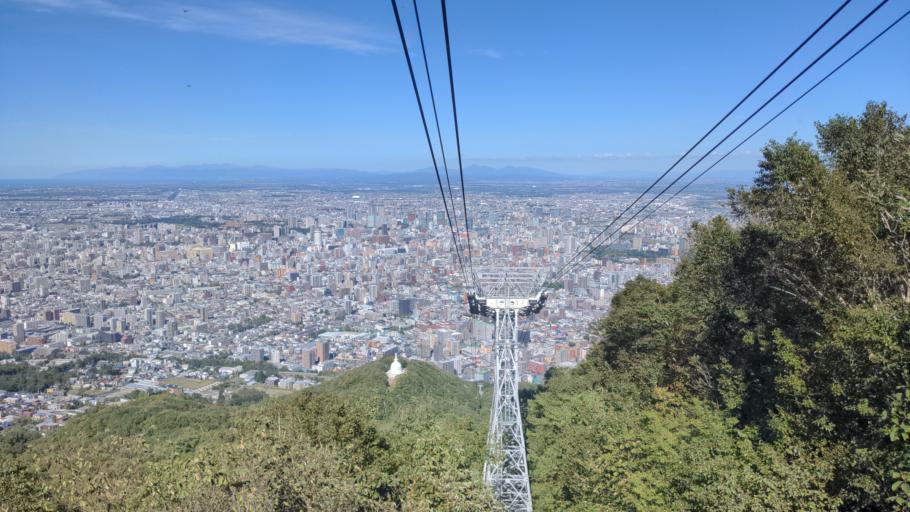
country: JP
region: Hokkaido
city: Sapporo
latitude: 43.0231
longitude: 141.3262
